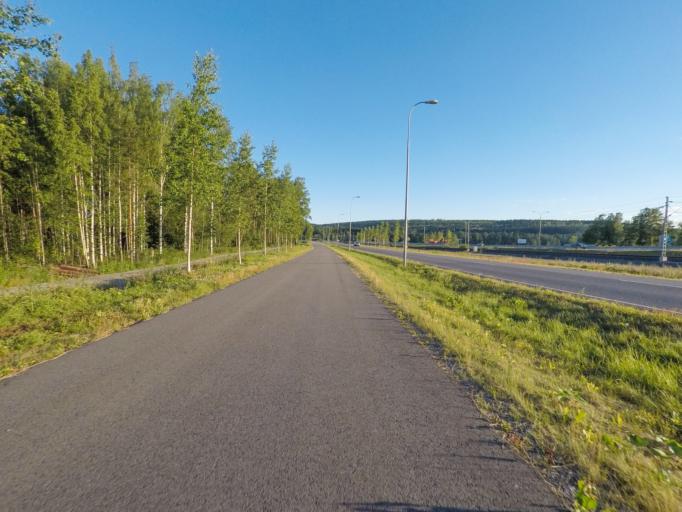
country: FI
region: Northern Savo
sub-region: Kuopio
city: Kuopio
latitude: 62.9435
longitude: 27.6703
